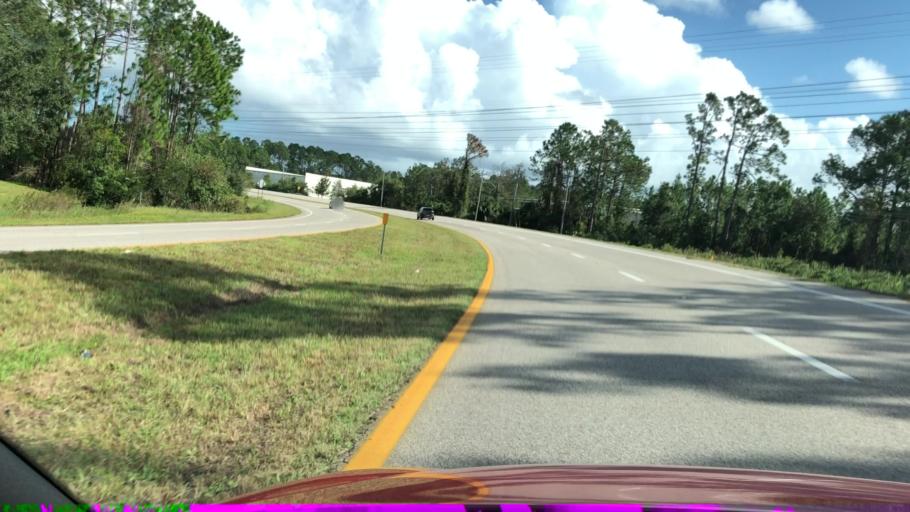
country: US
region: Florida
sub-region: Volusia County
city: Holly Hill
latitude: 29.2160
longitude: -81.0797
